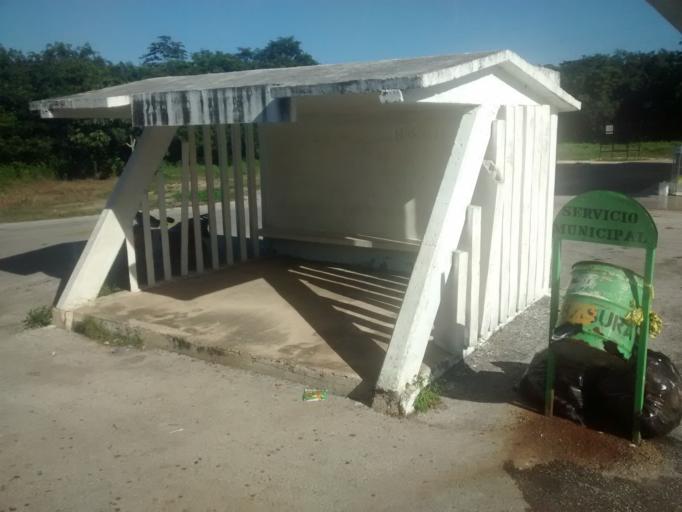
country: MX
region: Quintana Roo
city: Coba
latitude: 20.5084
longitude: -87.7187
